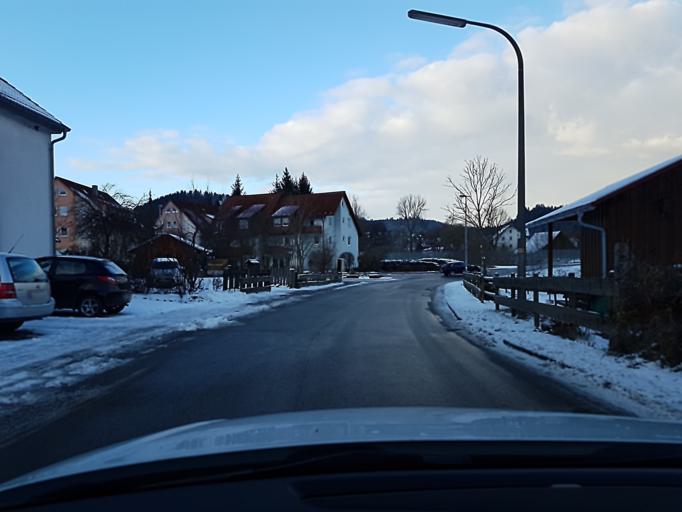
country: DE
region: Baden-Wuerttemberg
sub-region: Regierungsbezirk Stuttgart
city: Fichtenberg
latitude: 48.9834
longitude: 9.7117
